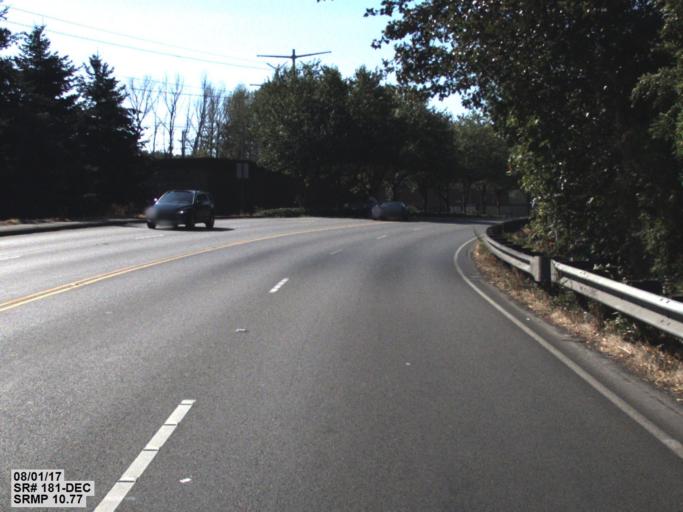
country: US
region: Washington
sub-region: King County
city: Tukwila
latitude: 47.4554
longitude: -122.2434
